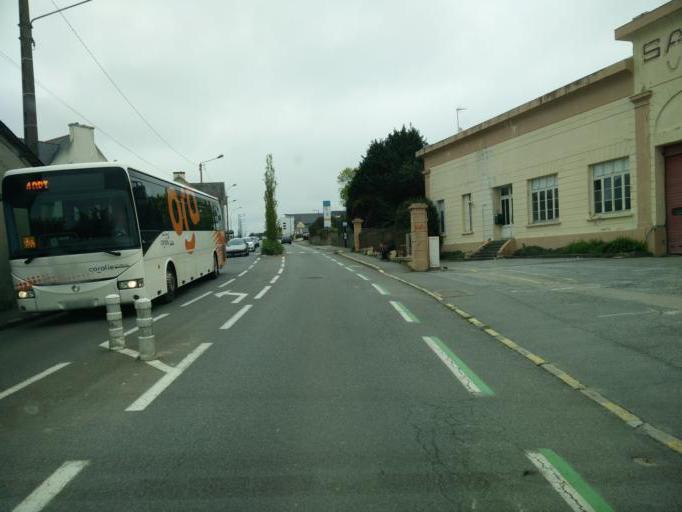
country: FR
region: Brittany
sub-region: Departement du Finistere
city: Concarneau
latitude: 47.8809
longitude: -3.9196
